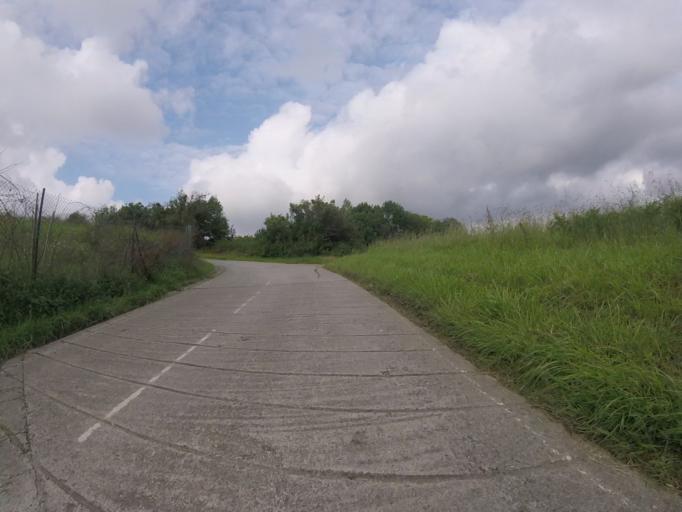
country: ES
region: Basque Country
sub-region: Provincia de Guipuzcoa
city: Astigarraga
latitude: 43.3052
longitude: -1.9450
